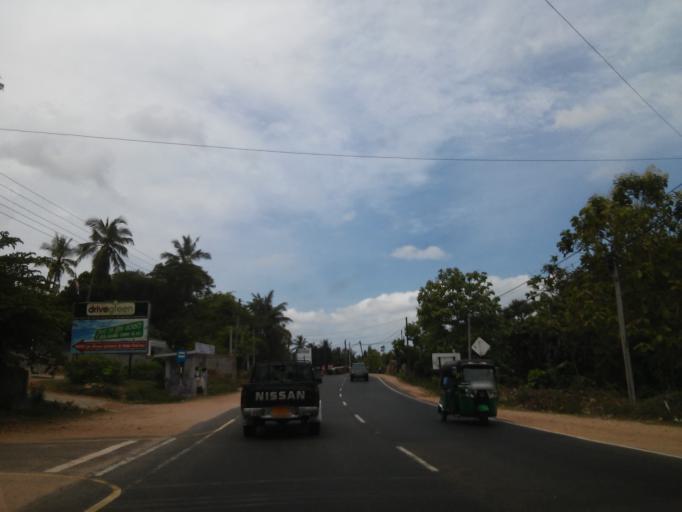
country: LK
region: Eastern Province
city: Trincomalee
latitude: 8.5874
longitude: 81.1981
